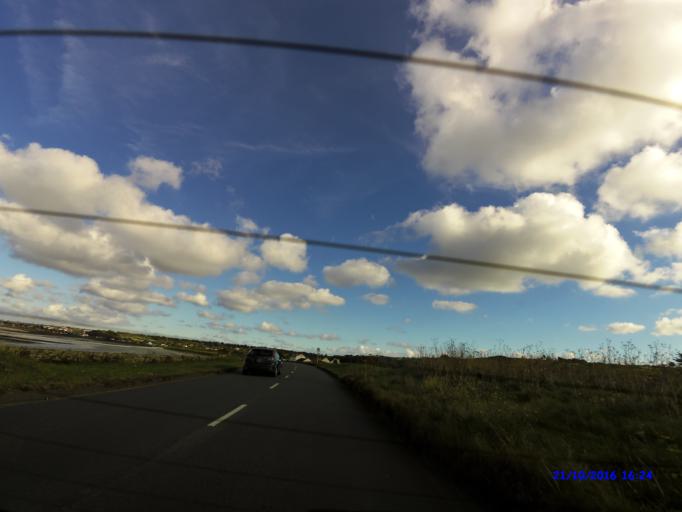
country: GG
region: St Peter Port
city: Saint Peter Port
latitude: 49.4632
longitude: -2.6231
